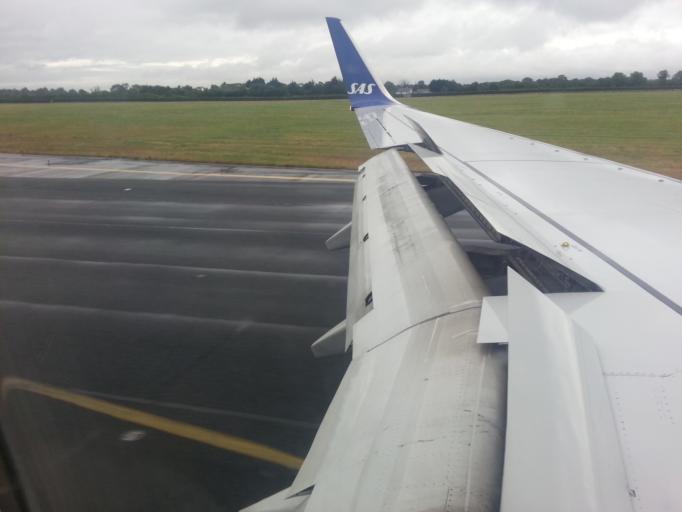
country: IE
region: Leinster
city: Ballymun
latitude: 53.4218
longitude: -6.2772
